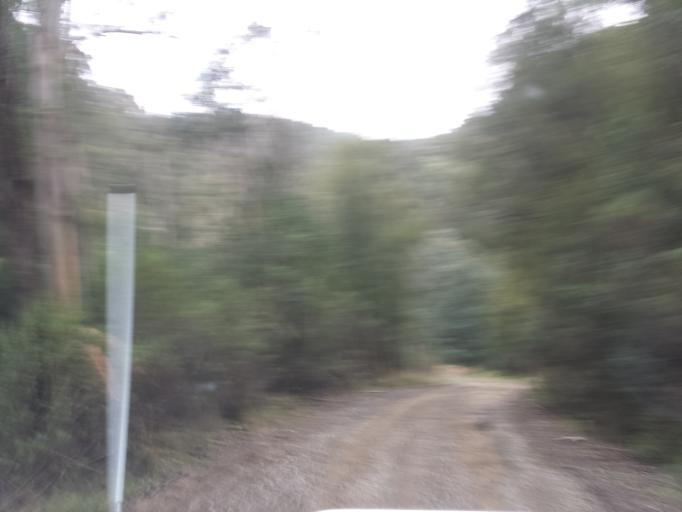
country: AU
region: Victoria
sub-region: Latrobe
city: Traralgon
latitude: -37.9530
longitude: 146.4522
